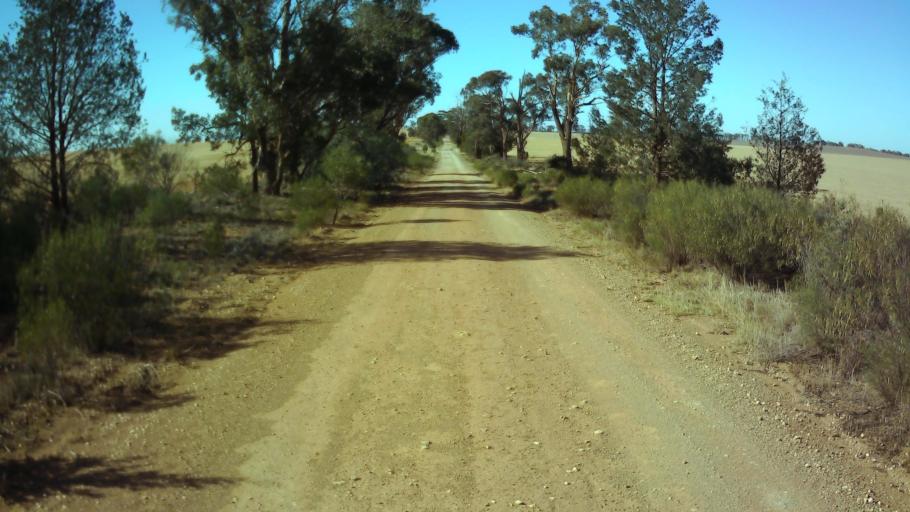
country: AU
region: New South Wales
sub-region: Weddin
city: Grenfell
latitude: -33.8841
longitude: 147.8817
